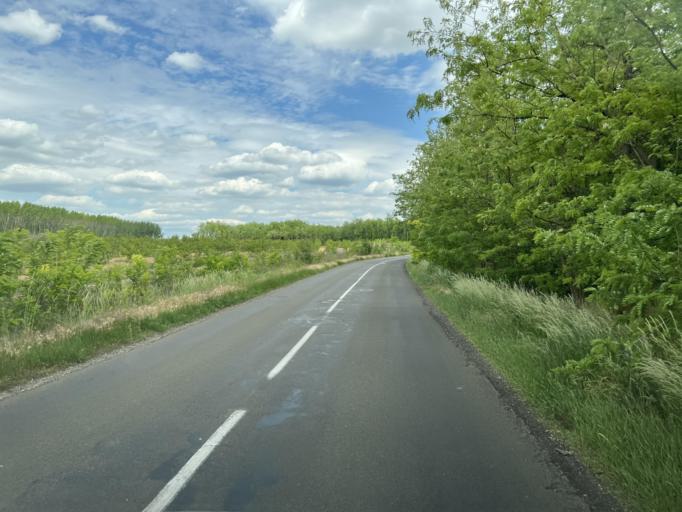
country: HU
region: Pest
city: Tapioszecso
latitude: 47.4716
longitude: 19.6212
